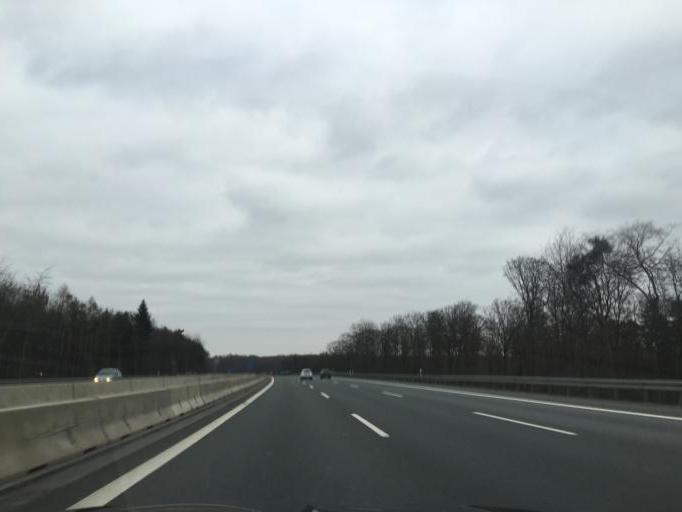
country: DE
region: Bavaria
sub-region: Regierungsbezirk Unterfranken
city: Uettingen
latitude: 49.7719
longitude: 9.7463
